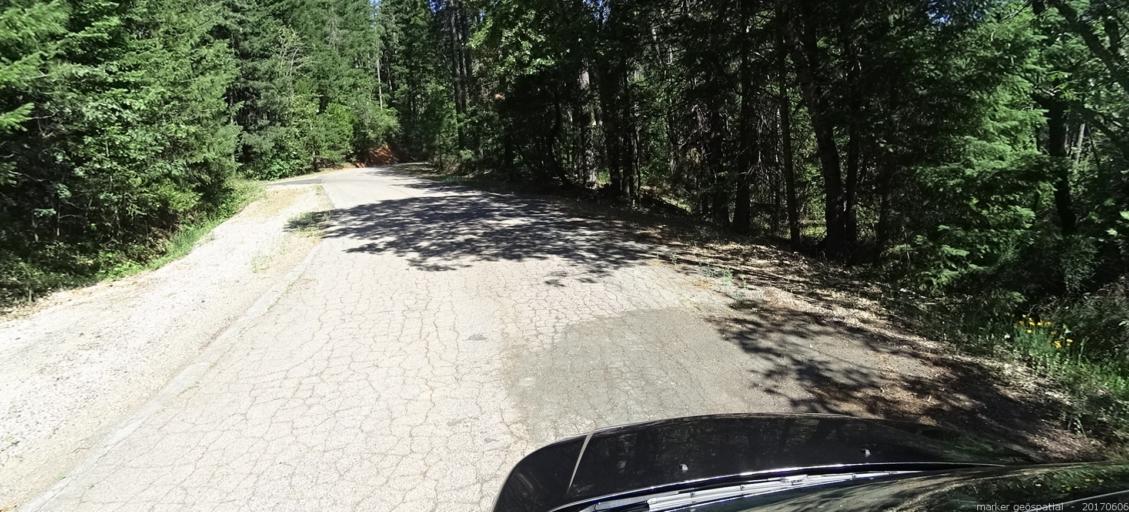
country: US
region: California
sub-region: Siskiyou County
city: Dunsmuir
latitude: 41.2019
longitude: -122.2790
